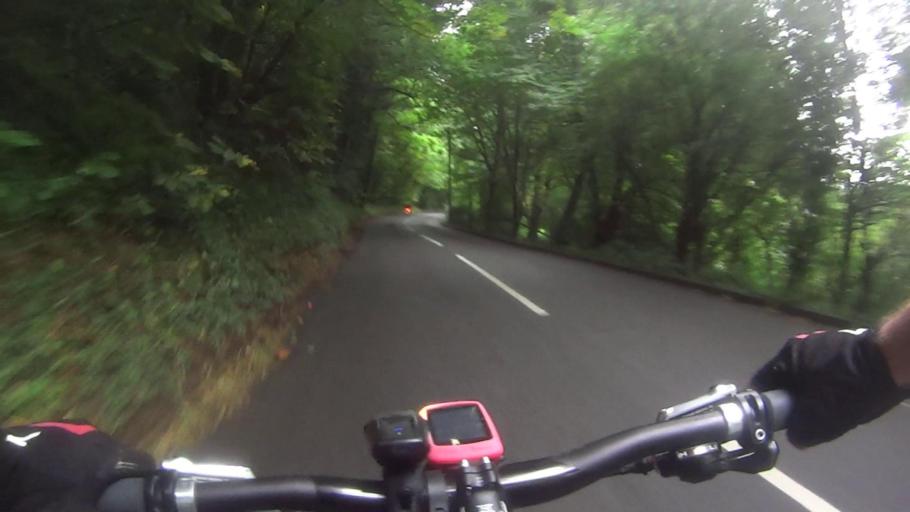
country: GB
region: England
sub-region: Worcestershire
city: Tenbury Wells
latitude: 52.3112
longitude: -2.5872
